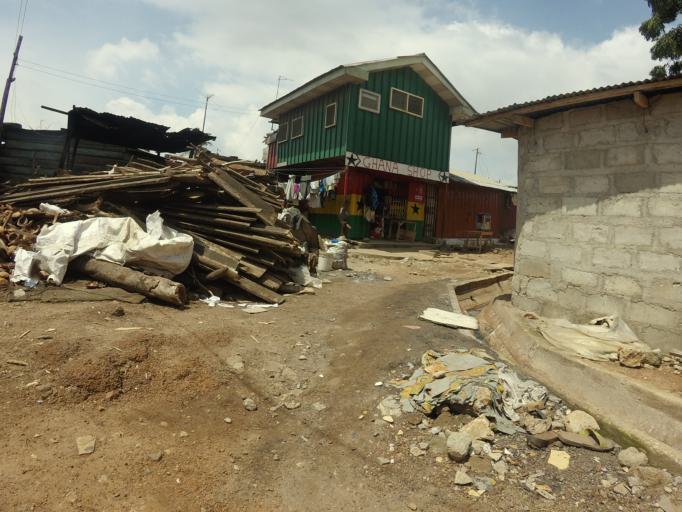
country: GH
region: Greater Accra
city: Accra
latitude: 5.5893
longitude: -0.2044
